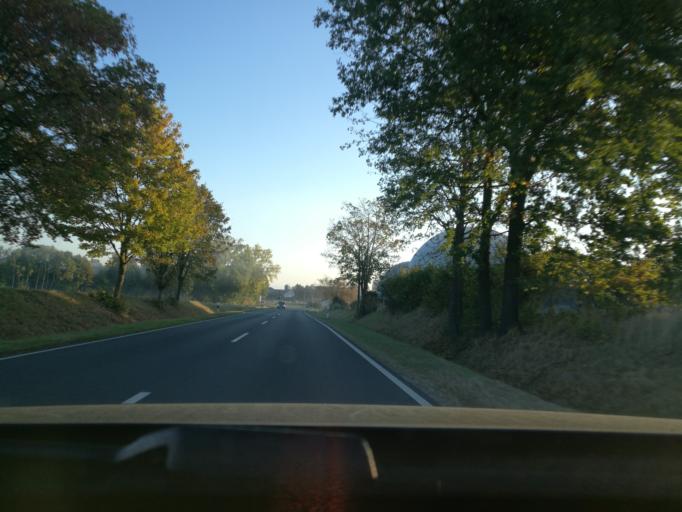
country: DE
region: Bavaria
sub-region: Regierungsbezirk Mittelfranken
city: Obermichelbach
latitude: 49.5281
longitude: 10.9187
